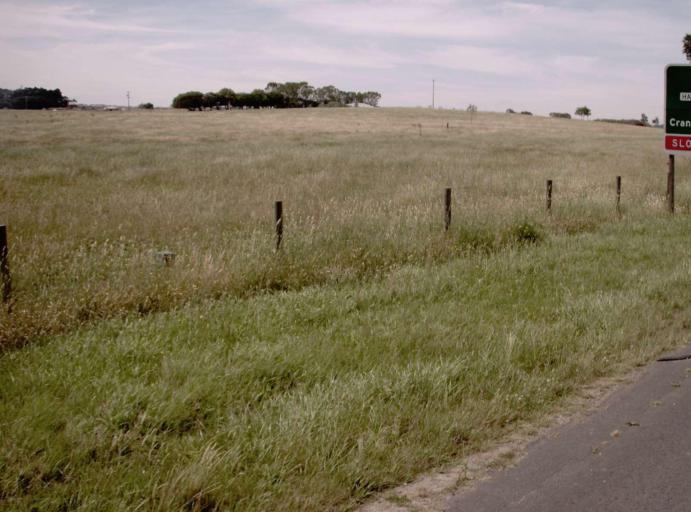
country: AU
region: Victoria
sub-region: Frankston
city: Skye
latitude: -38.1042
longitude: 145.2343
